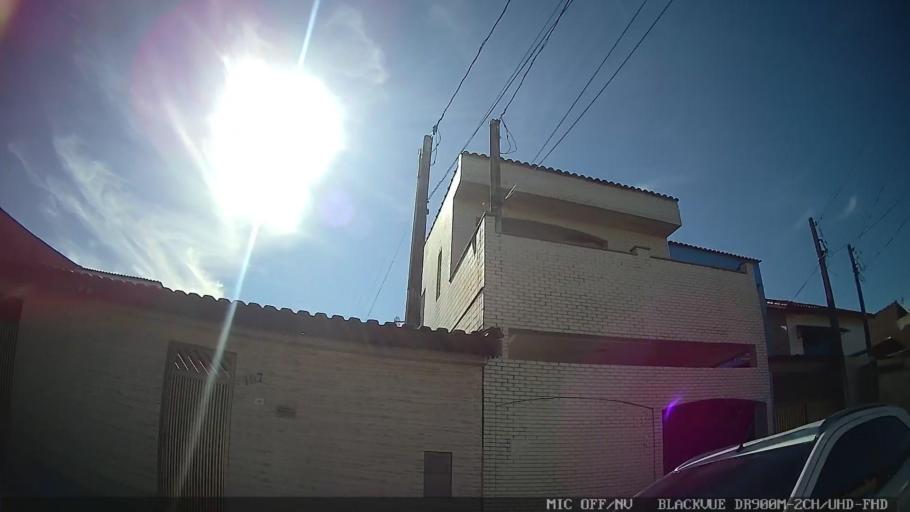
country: BR
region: Sao Paulo
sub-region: Santos
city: Santos
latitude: -23.9366
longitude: -46.2841
